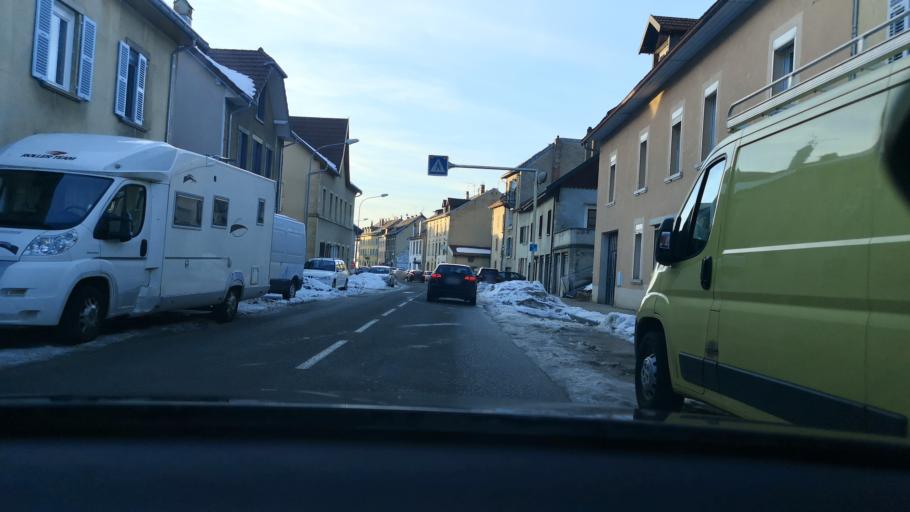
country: FR
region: Franche-Comte
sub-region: Departement du Doubs
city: Pontarlier
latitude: 46.9053
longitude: 6.3615
